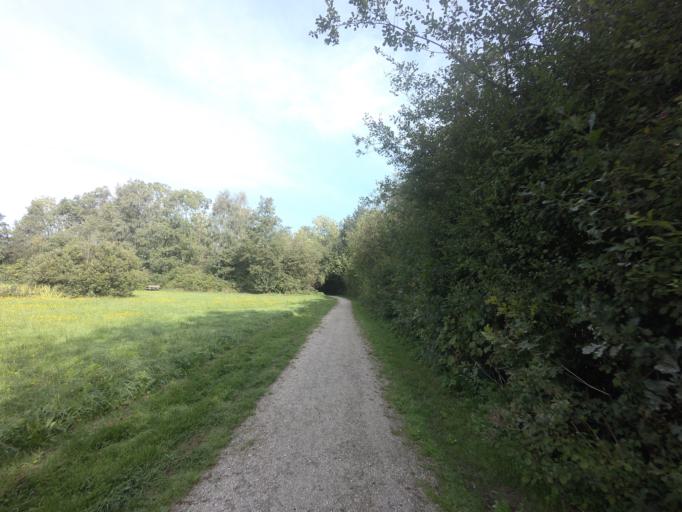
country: NL
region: Groningen
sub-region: Gemeente Zuidhorn
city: Grijpskerk
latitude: 53.2157
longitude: 6.3372
